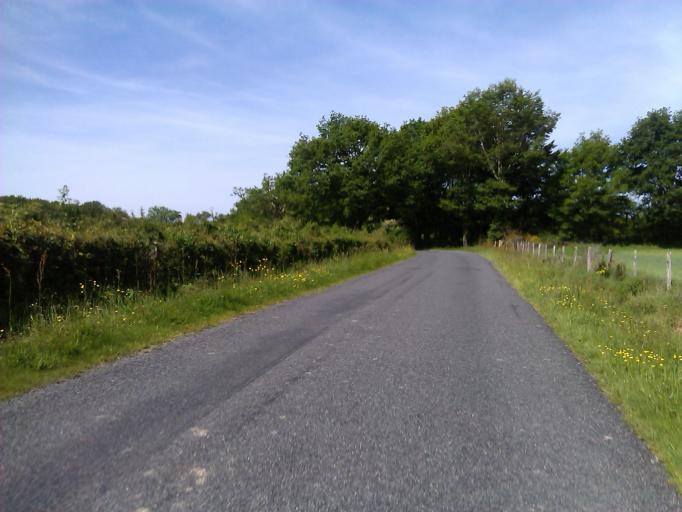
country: FR
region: Auvergne
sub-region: Departement de l'Allier
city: Yzeure
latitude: 46.5701
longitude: 3.4137
